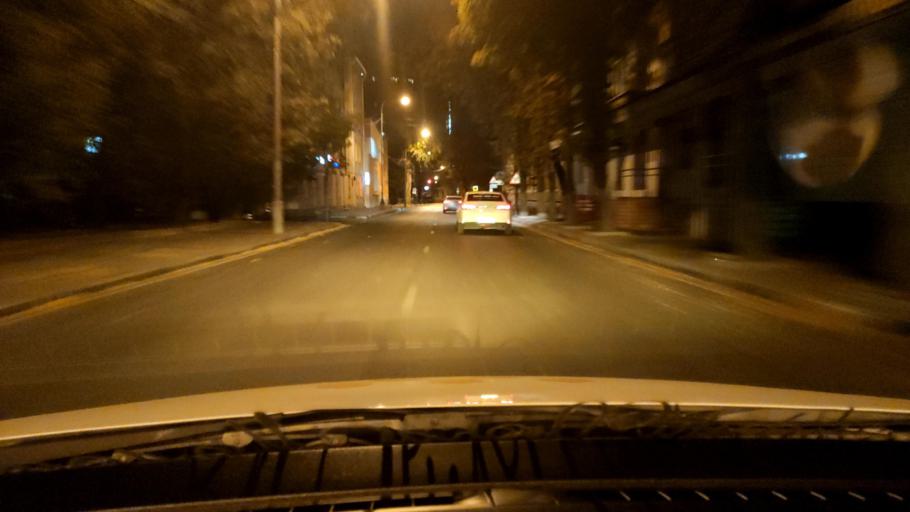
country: RU
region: Voronezj
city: Voronezh
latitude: 51.6655
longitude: 39.2004
